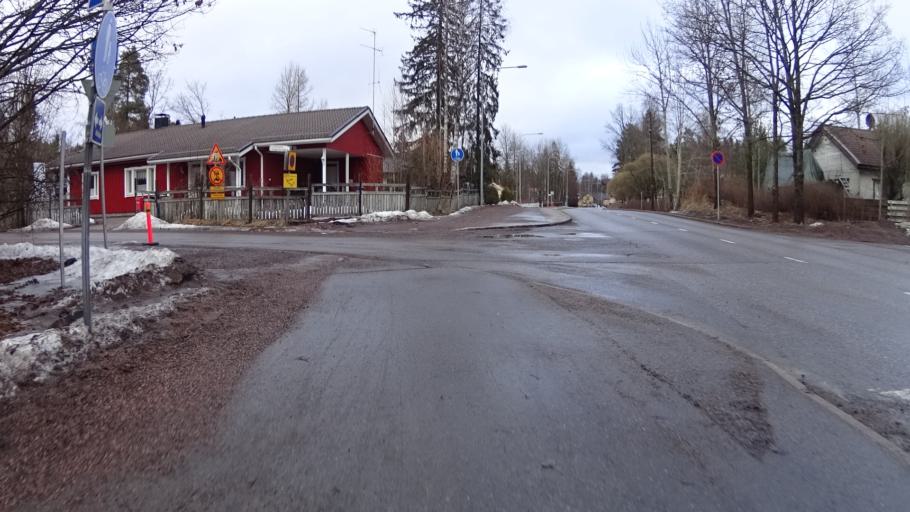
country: FI
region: Uusimaa
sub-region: Helsinki
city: Kilo
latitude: 60.2341
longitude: 24.7544
